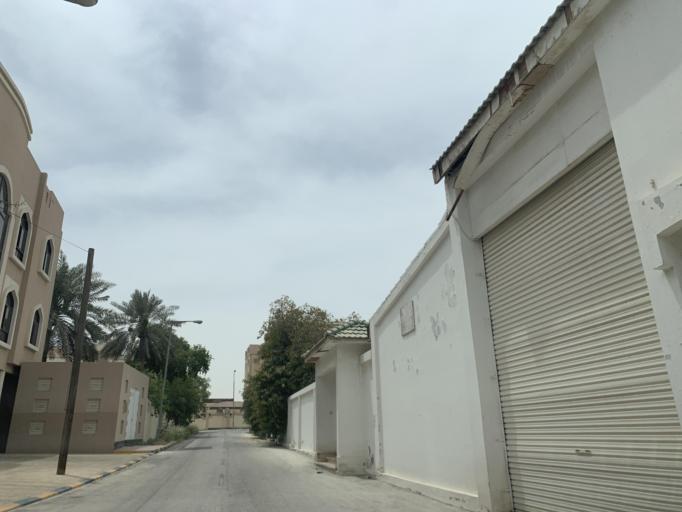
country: BH
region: Northern
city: Ar Rifa'
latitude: 26.1360
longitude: 50.5452
